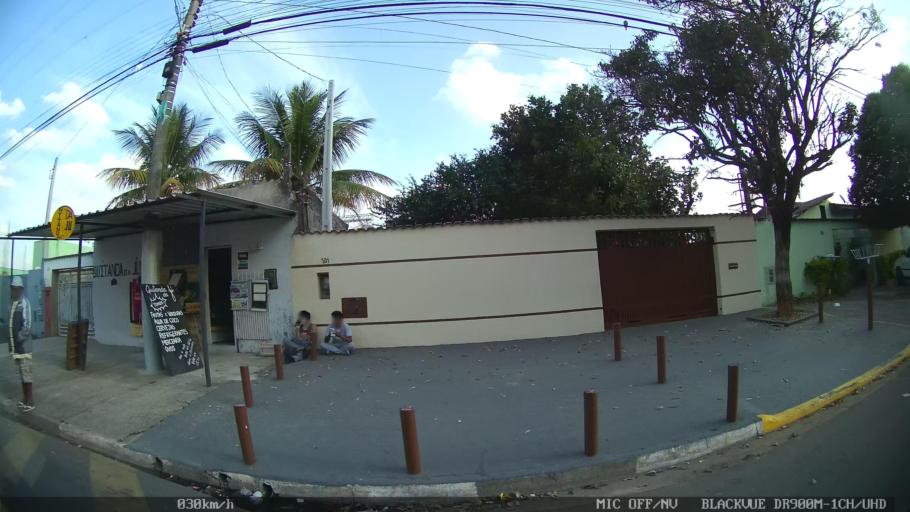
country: BR
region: Sao Paulo
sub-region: Hortolandia
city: Hortolandia
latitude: -22.8770
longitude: -47.1721
